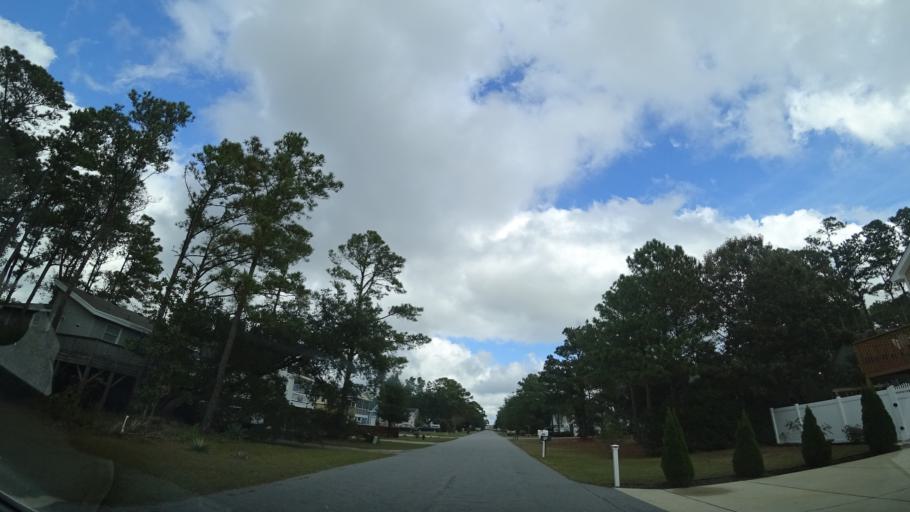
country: US
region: North Carolina
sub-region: Dare County
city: Kill Devil Hills
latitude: 35.9939
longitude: -75.6576
